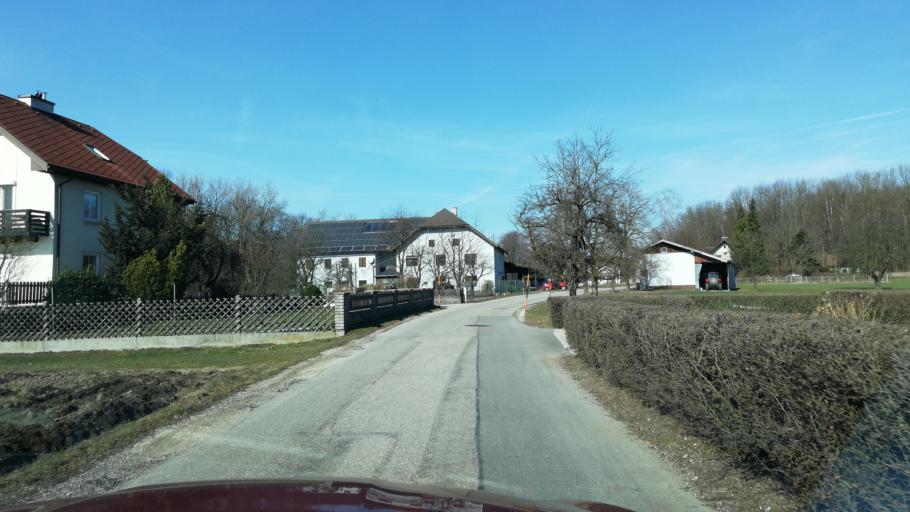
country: AT
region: Upper Austria
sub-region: Politischer Bezirk Vocklabruck
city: Lenzing
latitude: 47.9751
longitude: 13.6304
